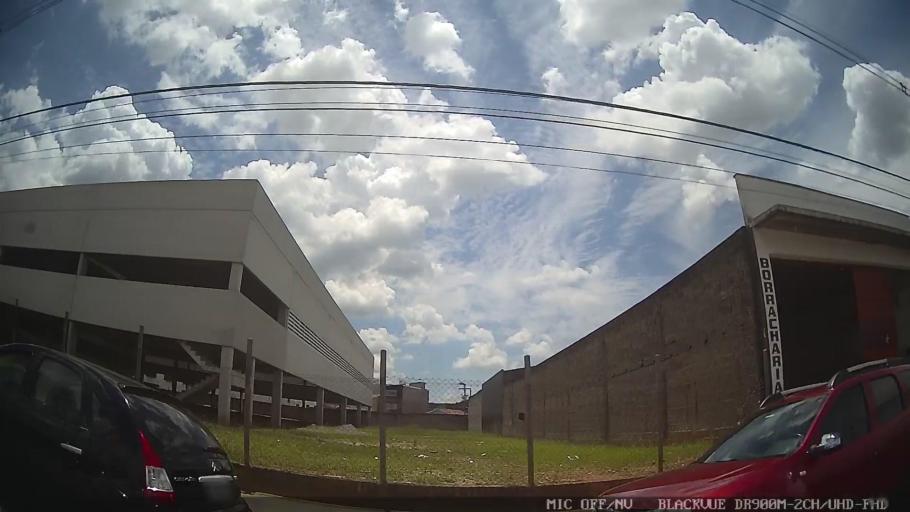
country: BR
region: Sao Paulo
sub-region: Atibaia
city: Atibaia
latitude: -23.1141
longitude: -46.5656
